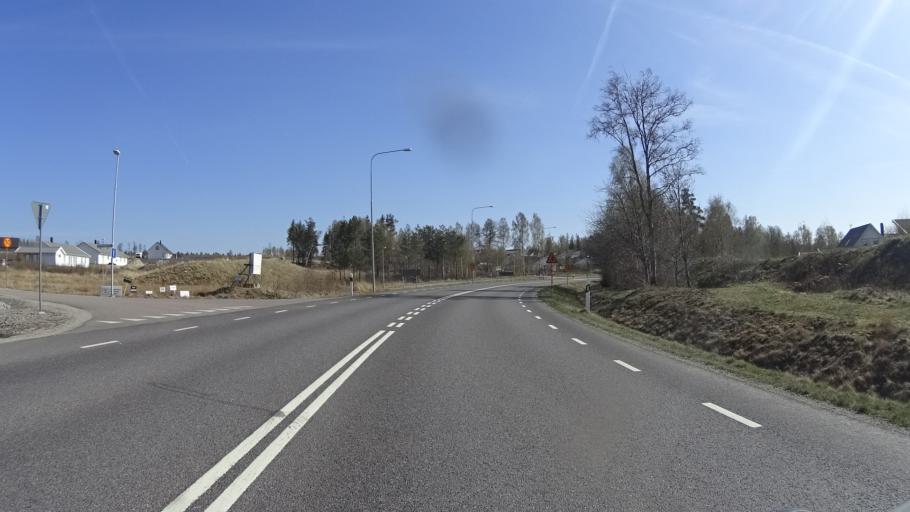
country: SE
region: Kronoberg
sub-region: Ljungby Kommun
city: Ljungby
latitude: 56.8414
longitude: 13.9742
